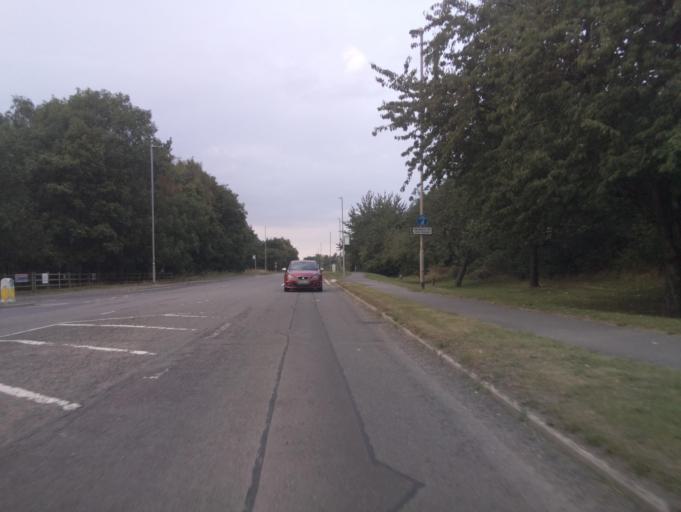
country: GB
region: England
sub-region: Nottinghamshire
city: South Collingham
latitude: 53.1501
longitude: -0.6700
